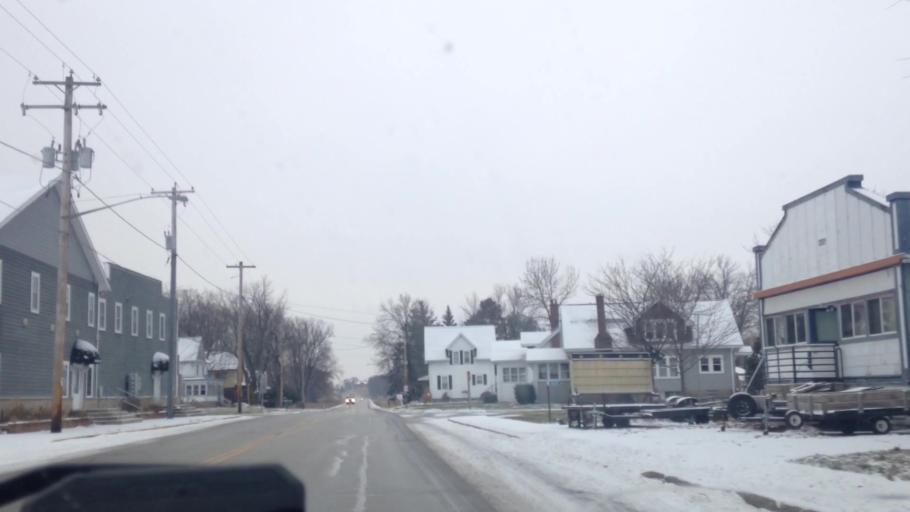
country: US
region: Wisconsin
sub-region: Waukesha County
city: Oconomowoc
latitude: 43.2107
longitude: -88.5158
